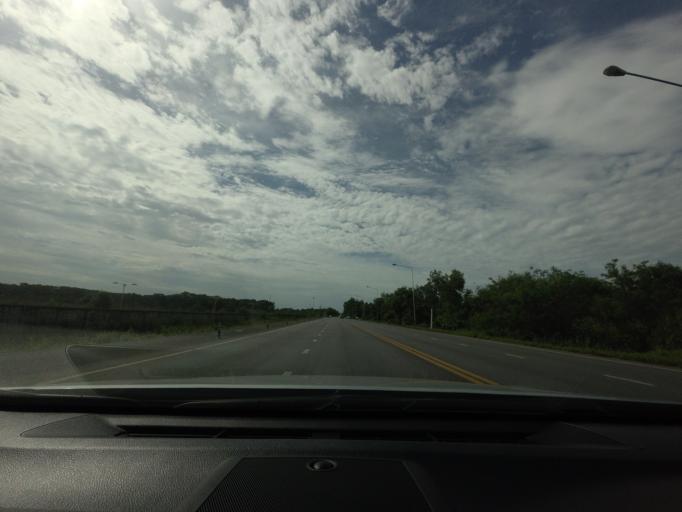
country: TH
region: Songkhla
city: Khlong Hoi Khong
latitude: 6.9362
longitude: 100.4154
